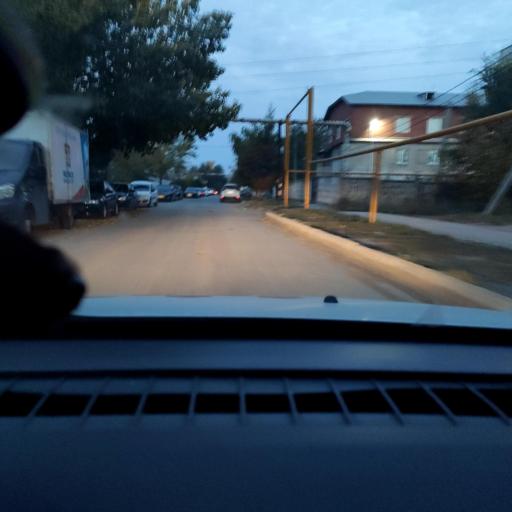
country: RU
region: Samara
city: Samara
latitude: 53.1069
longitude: 50.0825
